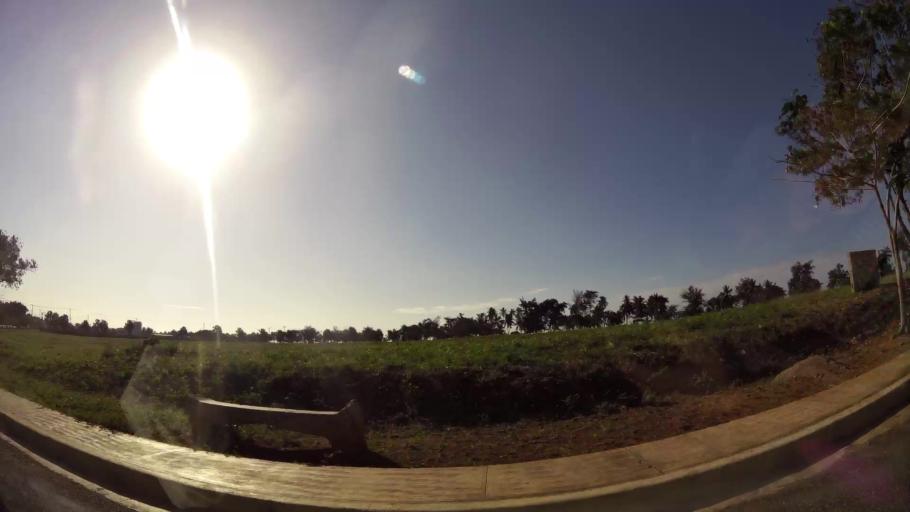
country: DO
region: Santo Domingo
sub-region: Santo Domingo
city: Santo Domingo Este
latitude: 18.4710
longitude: -69.8582
